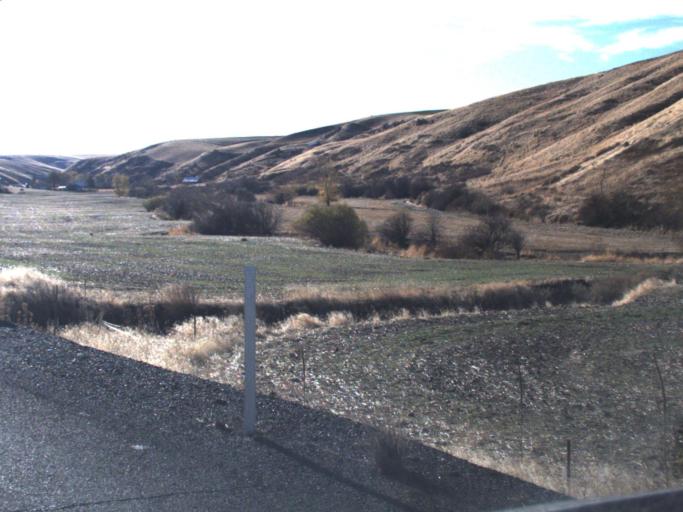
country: US
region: Washington
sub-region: Garfield County
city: Pomeroy
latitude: 46.4649
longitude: -117.4765
